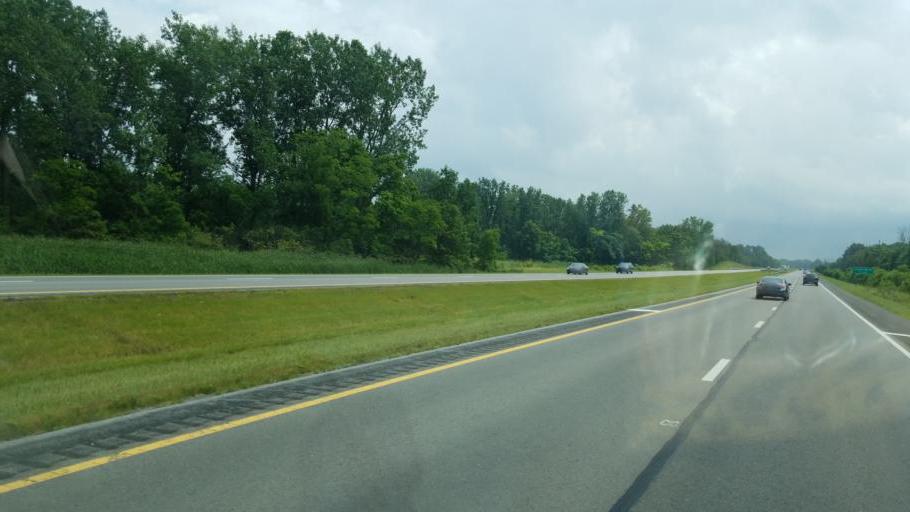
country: US
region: Ohio
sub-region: Logan County
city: Bellefontaine
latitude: 40.4200
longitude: -83.7961
